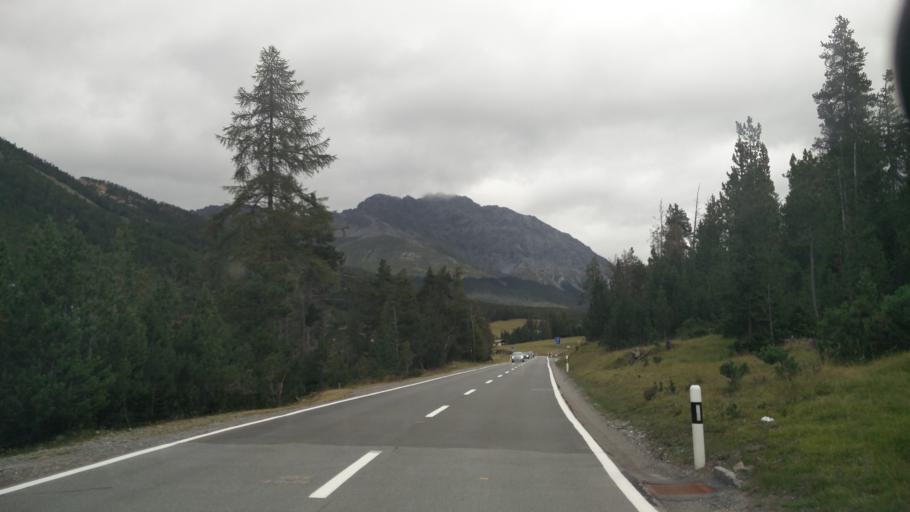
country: CH
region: Grisons
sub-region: Inn District
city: Zernez
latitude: 46.6638
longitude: 10.2038
